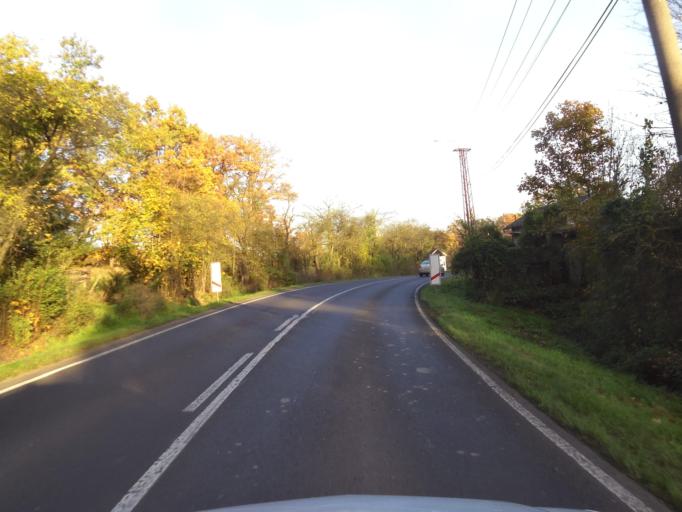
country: CZ
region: Liberecky
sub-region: Okres Ceska Lipa
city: Ceska Lipa
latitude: 50.6378
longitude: 14.5081
